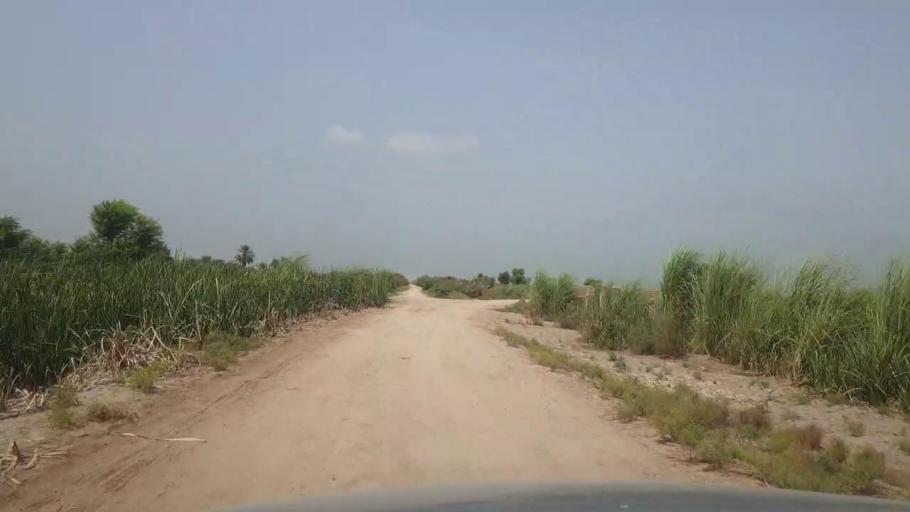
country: PK
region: Sindh
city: Garhi Yasin
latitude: 27.9571
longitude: 68.3604
